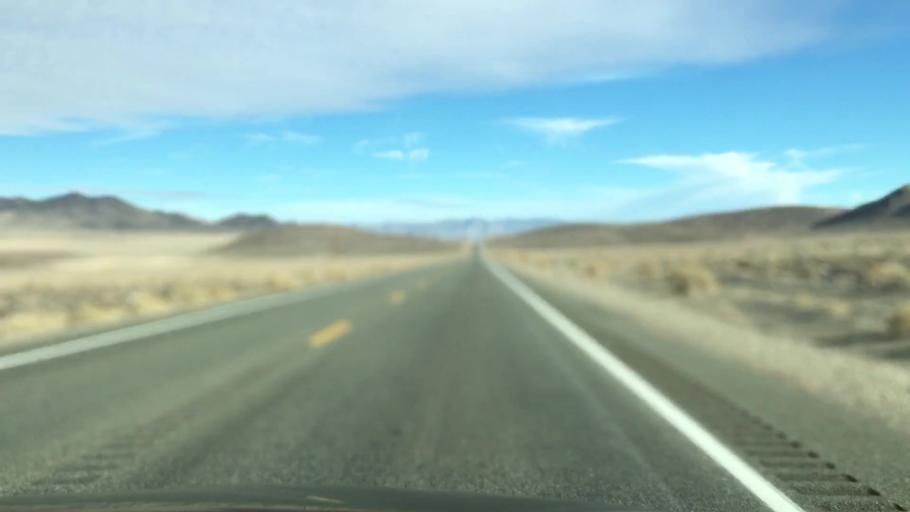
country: US
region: Nevada
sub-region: Mineral County
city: Hawthorne
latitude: 38.5500
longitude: -118.4576
